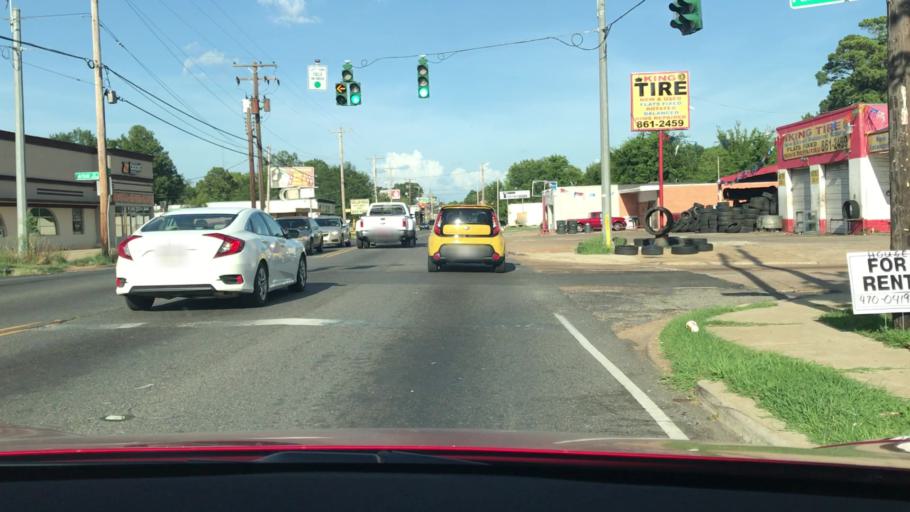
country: US
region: Louisiana
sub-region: Bossier Parish
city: Bossier City
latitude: 32.4420
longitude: -93.7504
